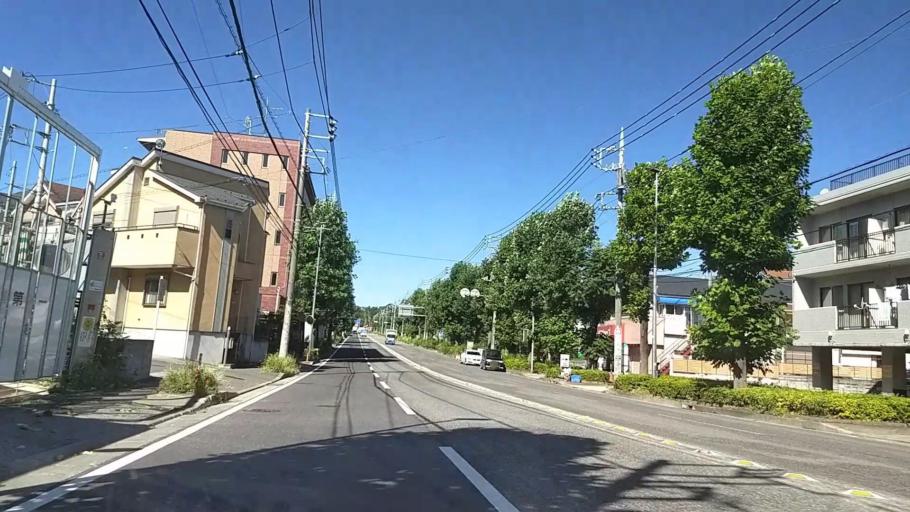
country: JP
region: Tokyo
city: Chofugaoka
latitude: 35.5929
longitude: 139.5446
